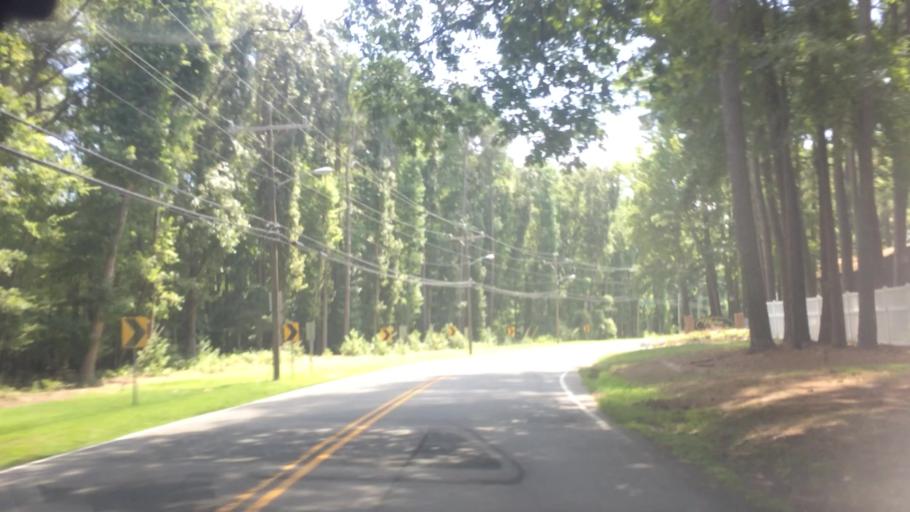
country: US
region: Virginia
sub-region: York County
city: Yorktown
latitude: 37.1998
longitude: -76.5725
